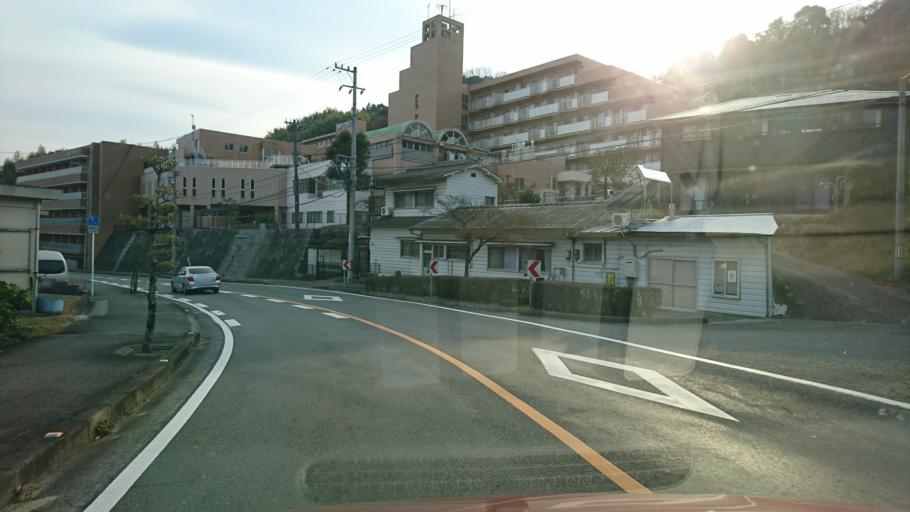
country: JP
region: Ehime
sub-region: Shikoku-chuo Shi
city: Matsuyama
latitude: 33.8649
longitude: 132.7734
